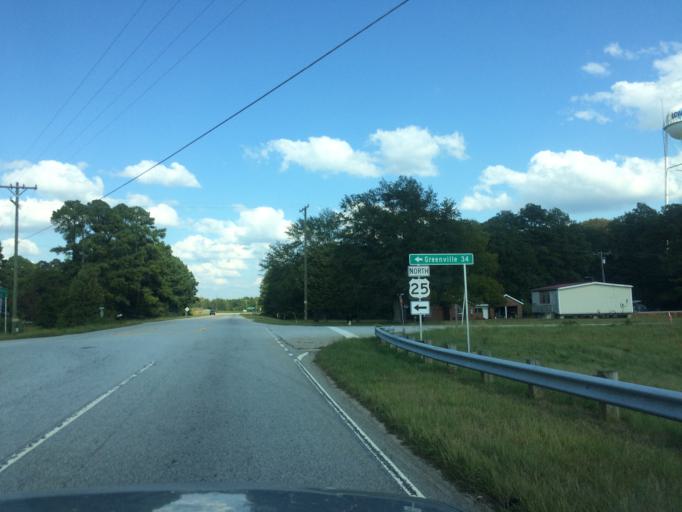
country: US
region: South Carolina
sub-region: Greenwood County
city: Ware Shoals
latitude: 34.4259
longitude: -82.2367
